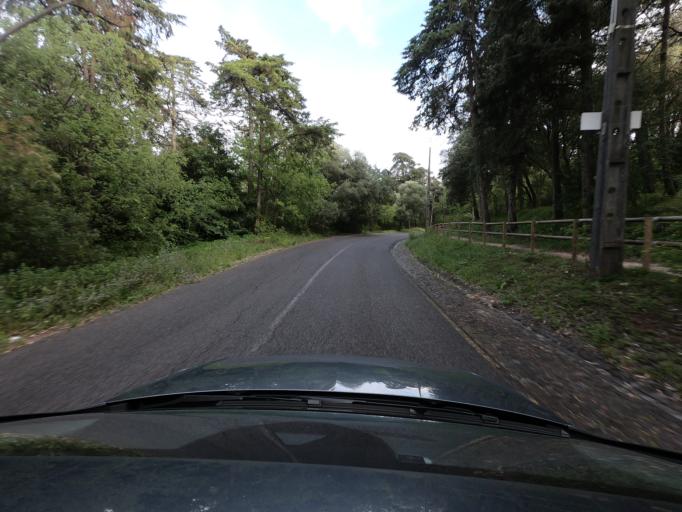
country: PT
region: Setubal
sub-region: Almada
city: Pragal
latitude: 38.7175
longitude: -9.1803
